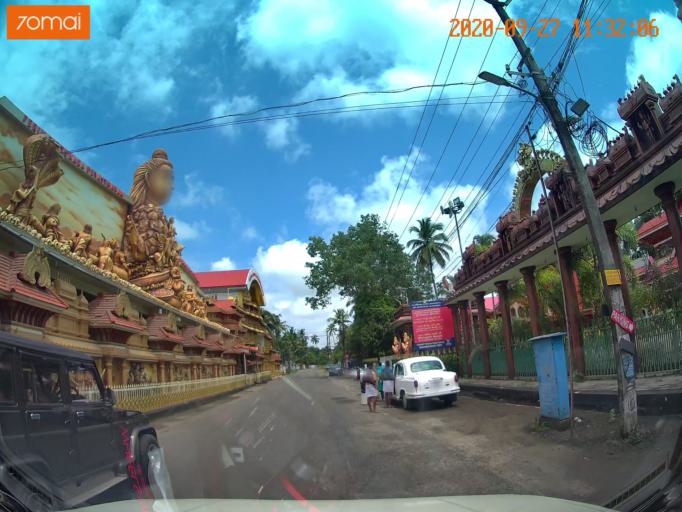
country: IN
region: Kerala
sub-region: Thrissur District
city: Thanniyam
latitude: 10.4253
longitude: 76.1313
